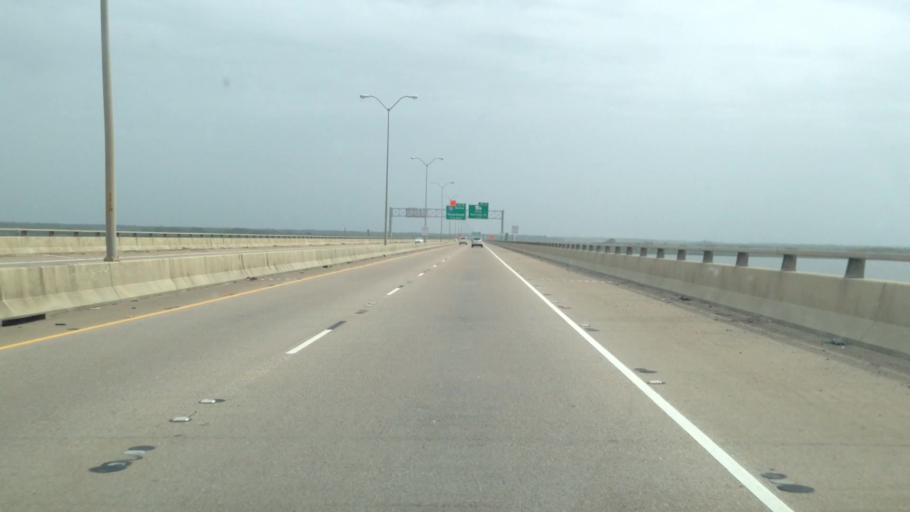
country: US
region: Louisiana
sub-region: Caddo Parish
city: Shreveport
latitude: 32.5059
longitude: -93.8159
